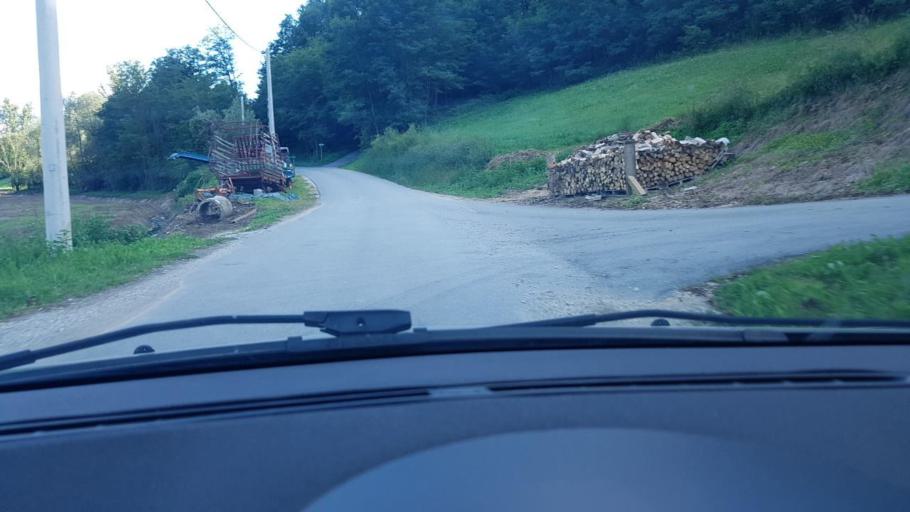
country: HR
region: Krapinsko-Zagorska
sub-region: Grad Krapina
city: Krapina
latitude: 46.1385
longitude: 15.8360
